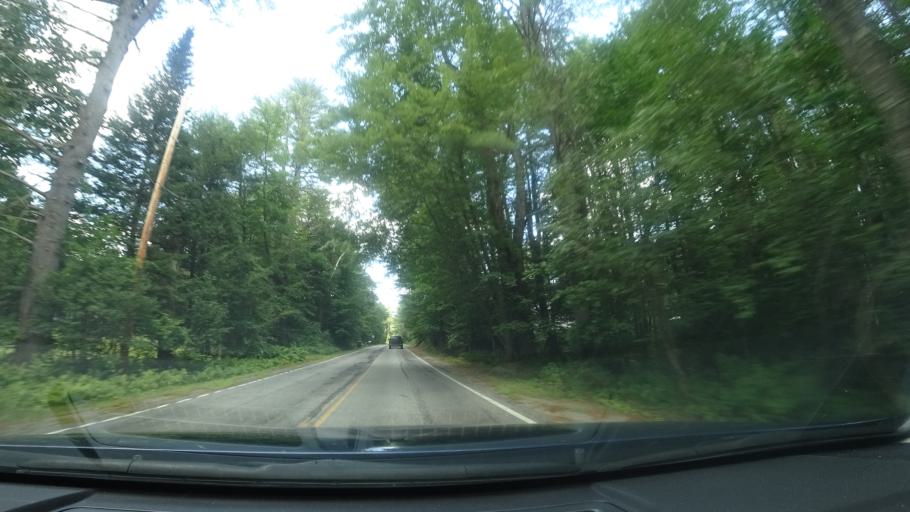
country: US
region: New York
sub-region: Warren County
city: Warrensburg
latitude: 43.6594
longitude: -73.8338
